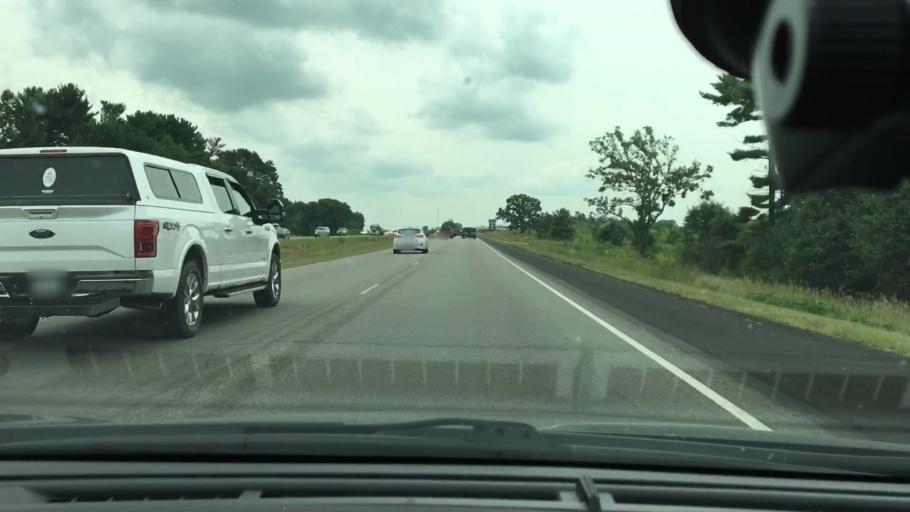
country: US
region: Minnesota
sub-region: Sherburne County
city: Zimmerman
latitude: 45.4516
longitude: -93.5860
